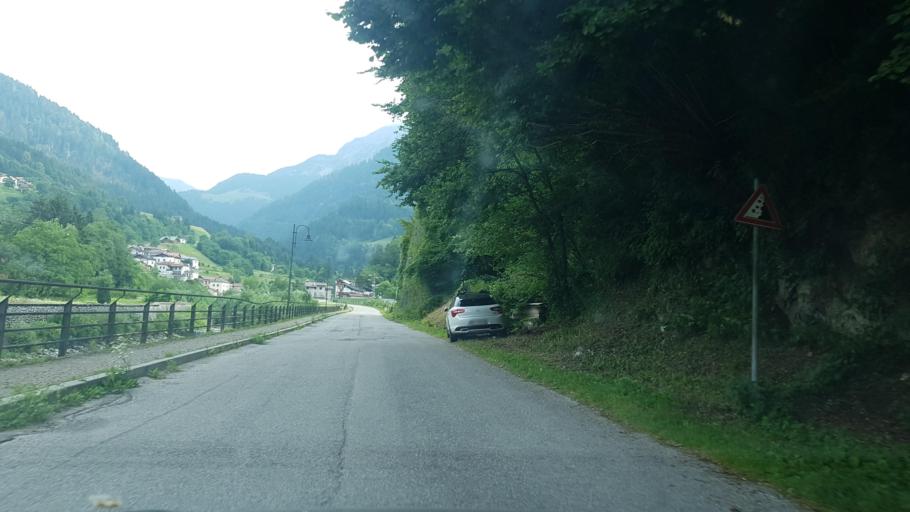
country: IT
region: Friuli Venezia Giulia
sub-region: Provincia di Udine
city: Paularo
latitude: 46.5323
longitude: 13.1177
